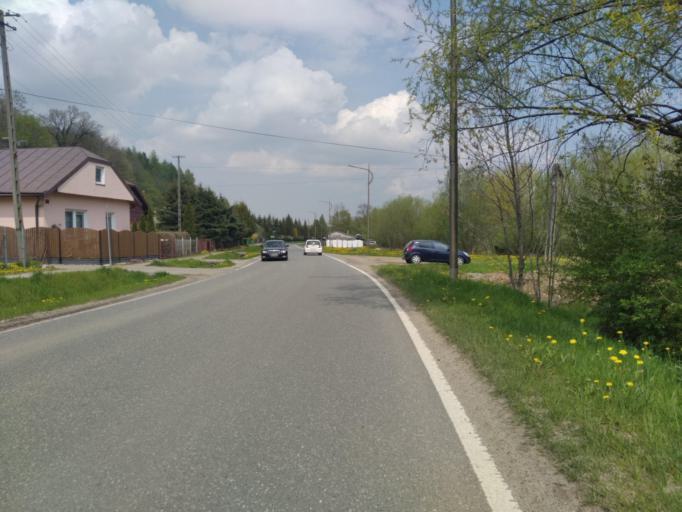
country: PL
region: Subcarpathian Voivodeship
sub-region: Powiat krosnienski
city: Rymanow
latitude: 49.5686
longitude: 21.8652
